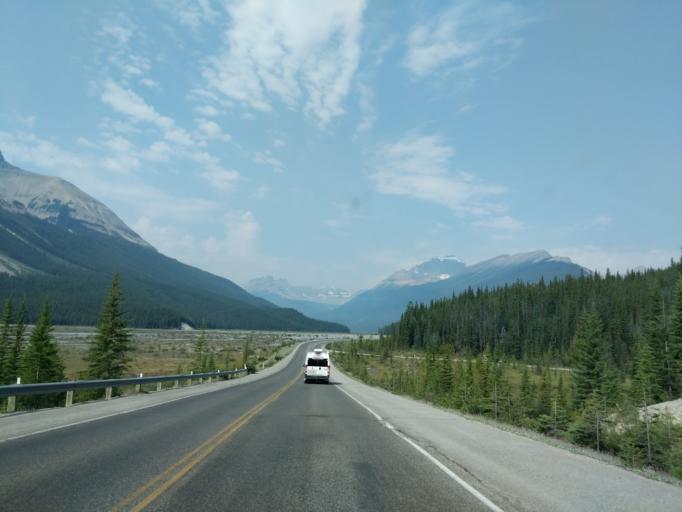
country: CA
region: British Columbia
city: Golden
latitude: 52.0683
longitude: -116.9065
